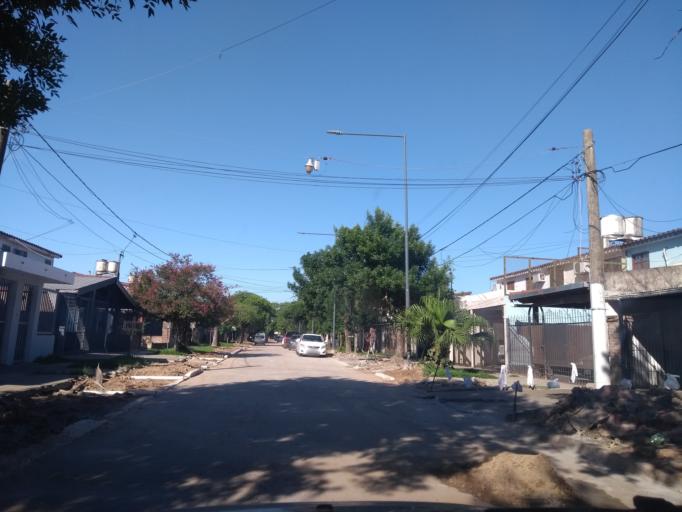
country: AR
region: Chaco
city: Resistencia
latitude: -27.4756
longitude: -58.9821
